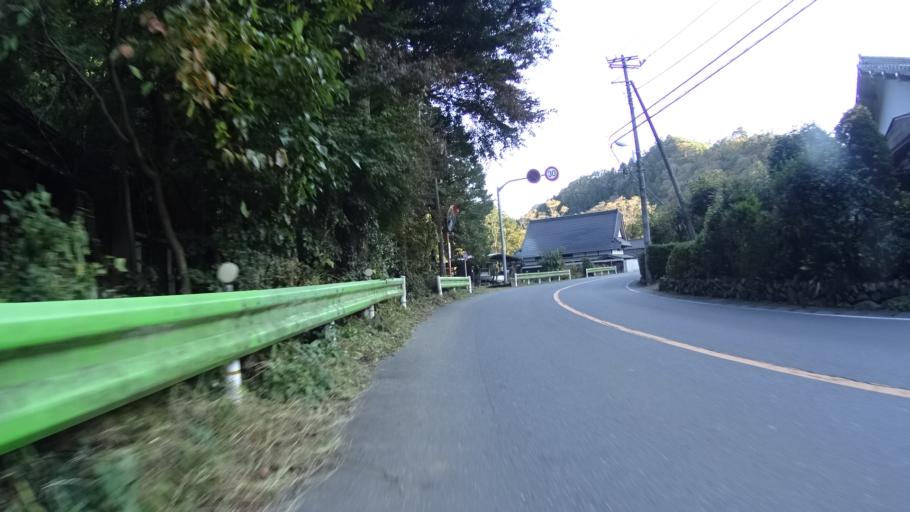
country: JP
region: Tokyo
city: Itsukaichi
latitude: 35.6698
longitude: 139.2338
